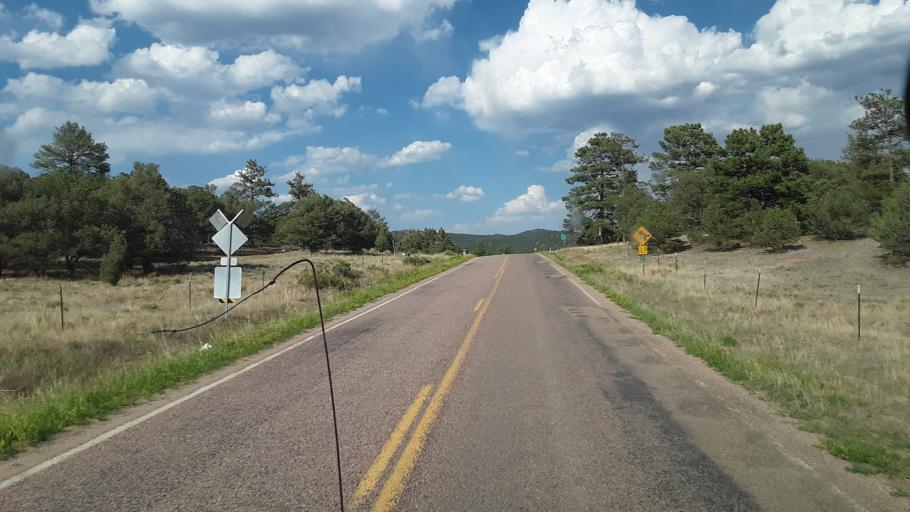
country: US
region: Colorado
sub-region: Custer County
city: Westcliffe
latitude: 38.3572
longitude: -105.4744
